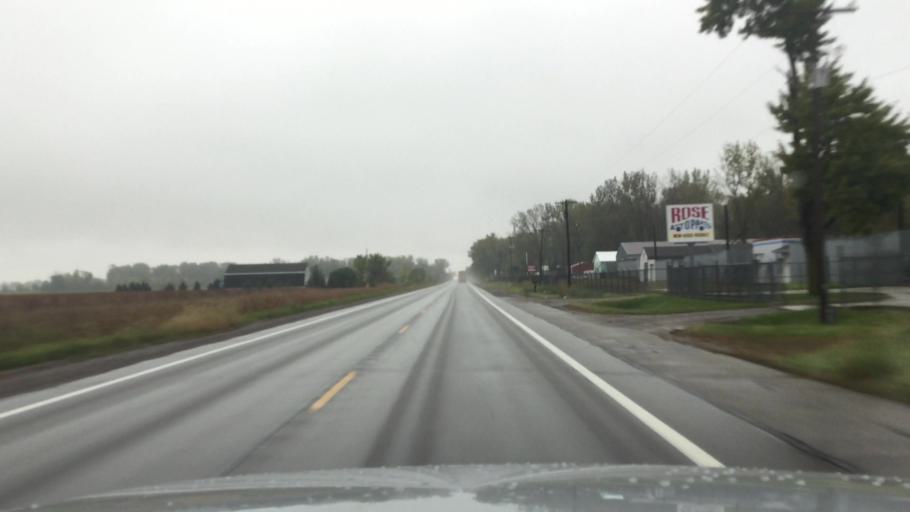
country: US
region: Michigan
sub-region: Saginaw County
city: Saginaw
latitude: 43.3761
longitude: -83.9552
